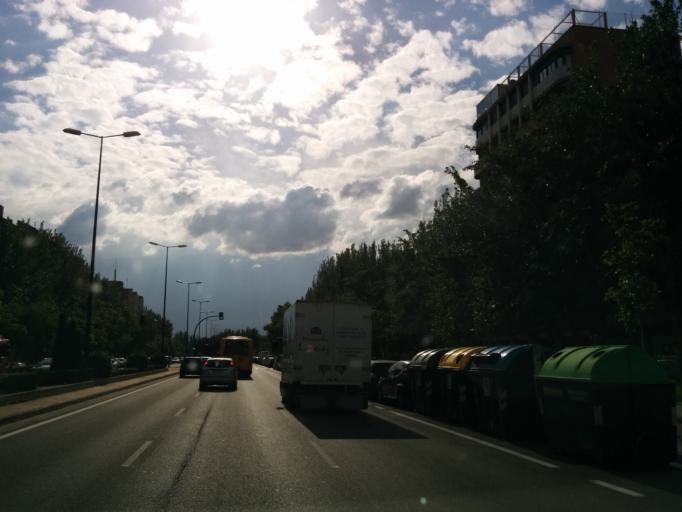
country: ES
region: Aragon
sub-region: Provincia de Zaragoza
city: Zaragoza
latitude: 41.6731
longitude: -0.8851
